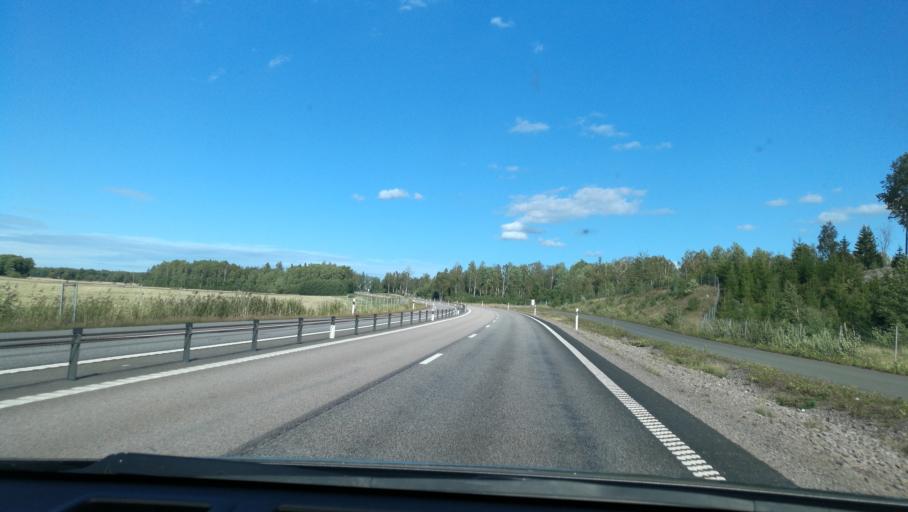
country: SE
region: Vaestra Goetaland
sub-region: Mariestads Kommun
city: Mariestad
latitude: 58.7565
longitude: 13.9658
